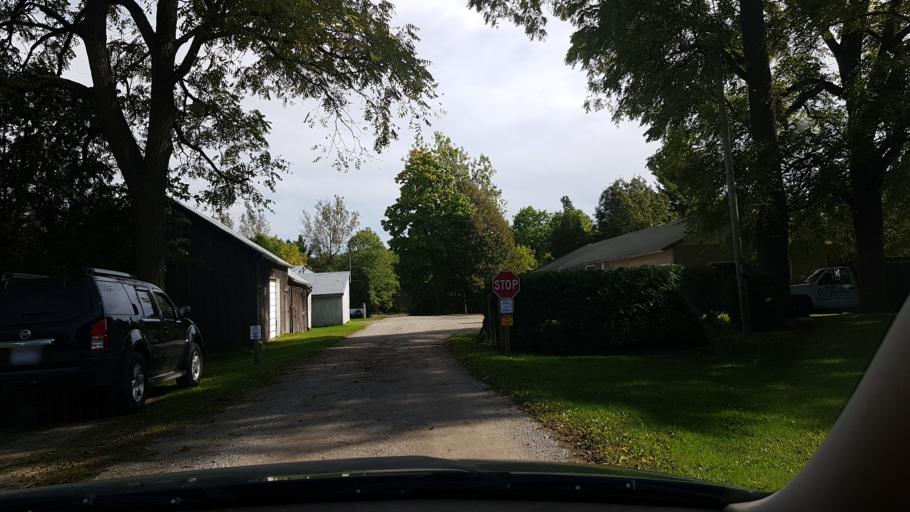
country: CA
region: Ontario
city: Delaware
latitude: 42.8847
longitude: -81.4804
